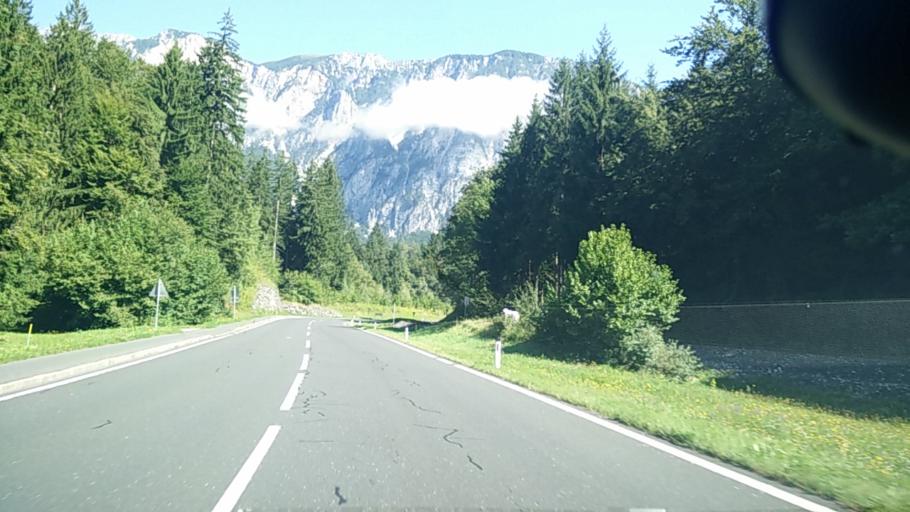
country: AT
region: Carinthia
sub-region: Politischer Bezirk Villach Land
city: Arnoldstein
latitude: 46.5623
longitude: 13.6940
